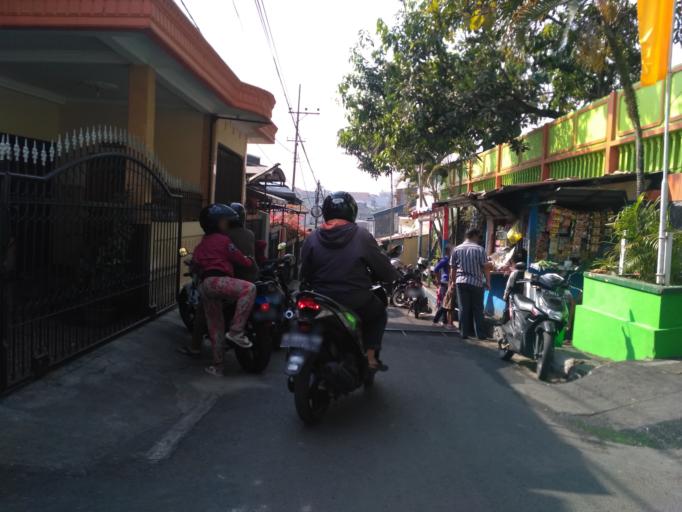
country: ID
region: East Java
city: Malang
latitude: -7.9797
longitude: 112.6217
